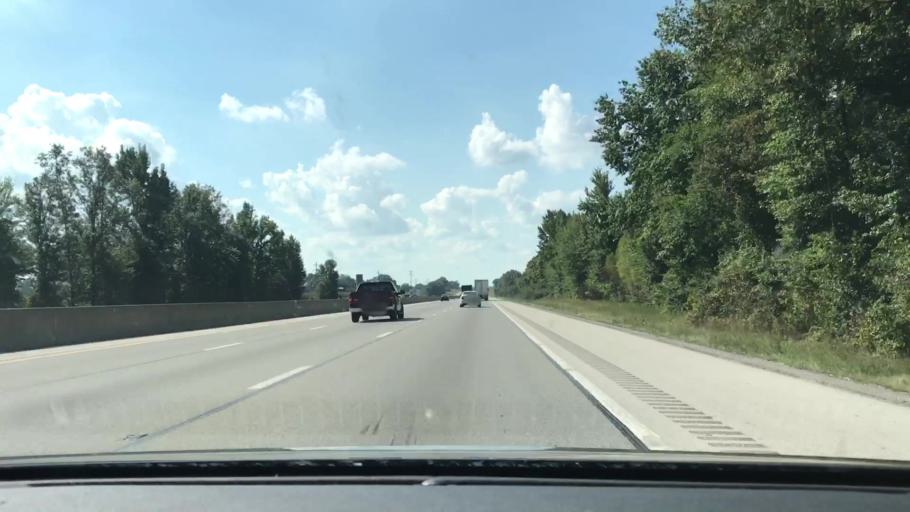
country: US
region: Kentucky
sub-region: Warren County
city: Plano
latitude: 36.8505
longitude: -86.4586
